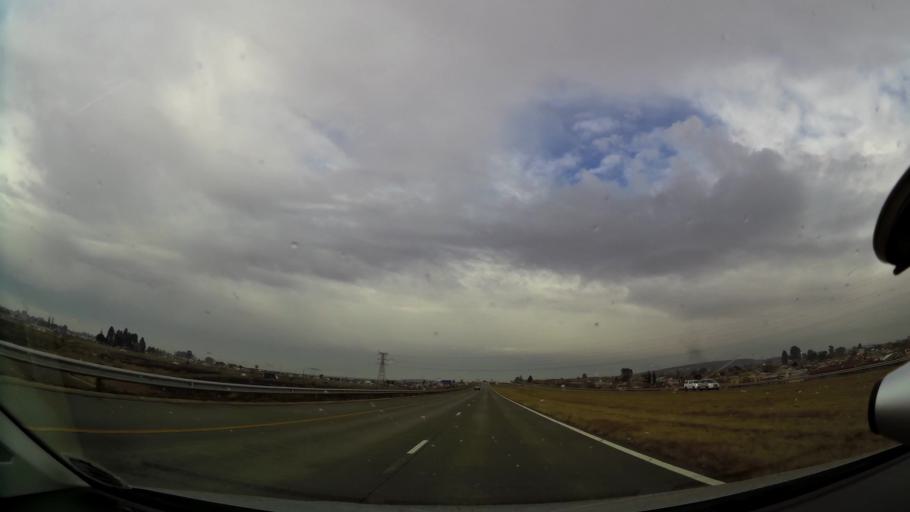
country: ZA
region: Gauteng
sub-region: City of Johannesburg Metropolitan Municipality
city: Orange Farm
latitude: -26.4239
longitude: 27.8747
